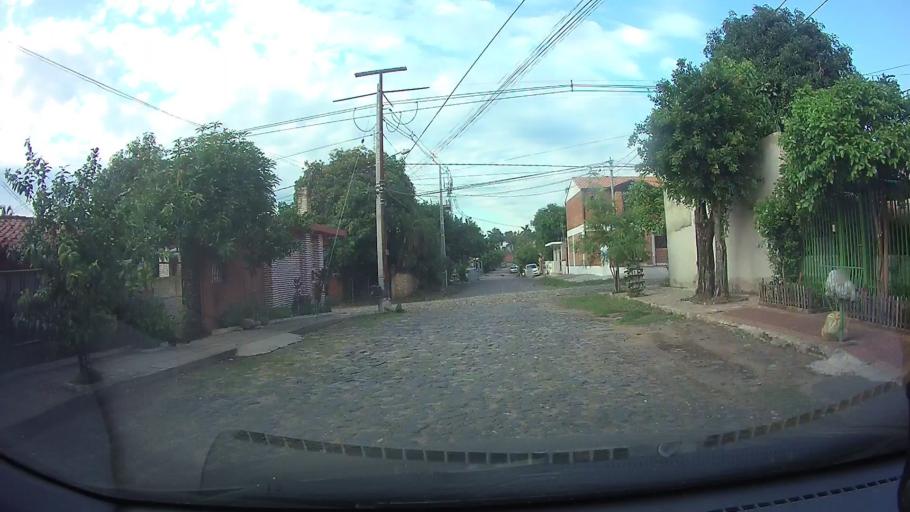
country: PY
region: Central
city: Fernando de la Mora
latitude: -25.2622
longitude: -57.5508
